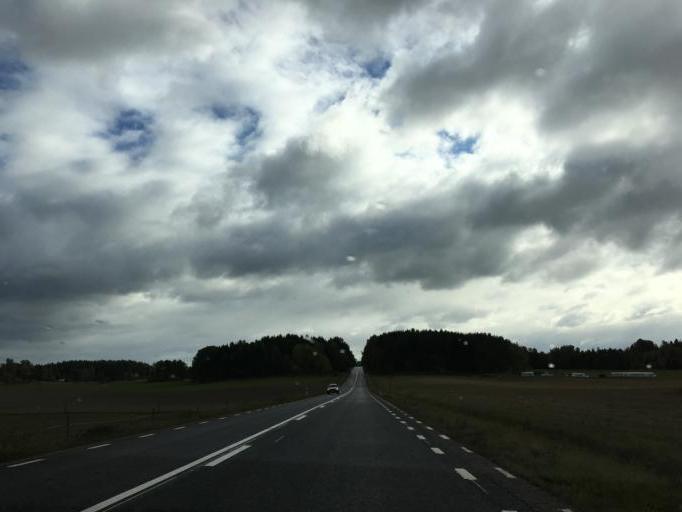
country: SE
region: Soedermanland
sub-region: Nykopings Kommun
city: Olstorp
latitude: 58.8742
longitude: 16.6770
